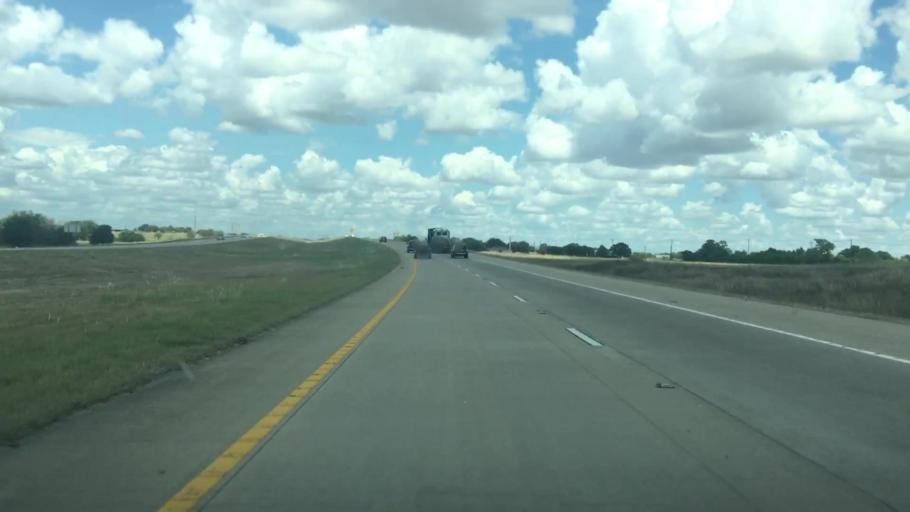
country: US
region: Texas
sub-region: Williamson County
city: Hutto
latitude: 30.5571
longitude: -97.5770
